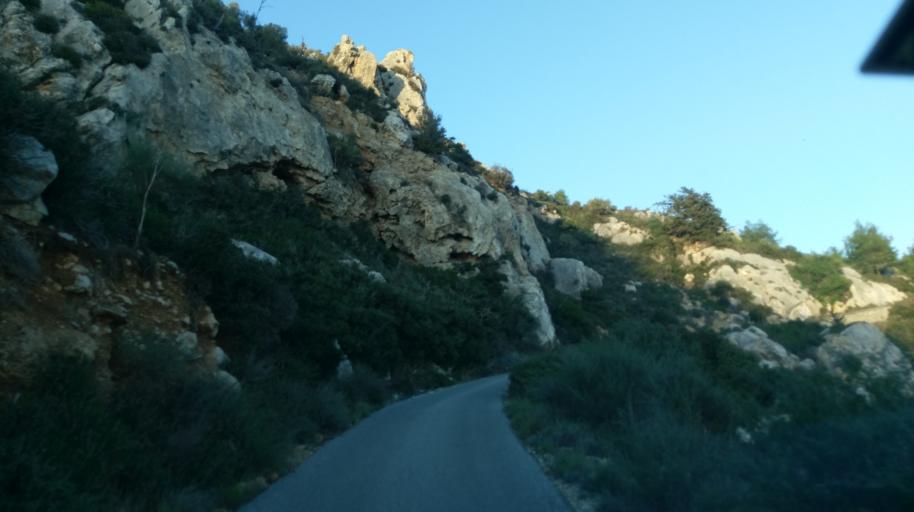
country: CY
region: Ammochostos
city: Trikomo
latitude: 35.4037
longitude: 33.9194
